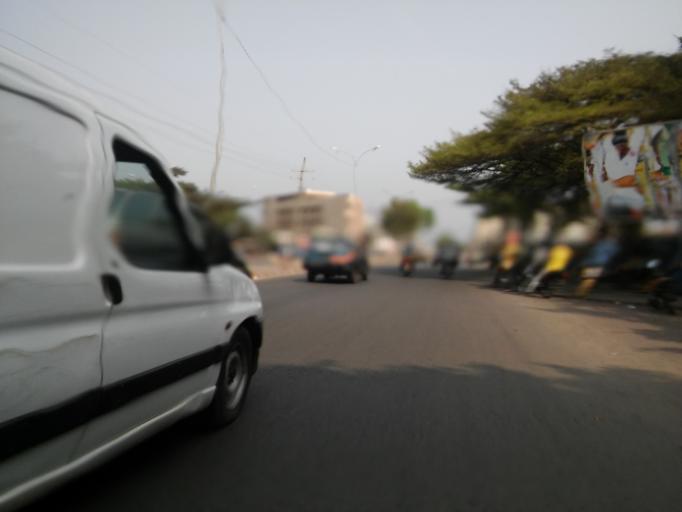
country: BJ
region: Littoral
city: Cotonou
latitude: 6.3706
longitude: 2.4191
